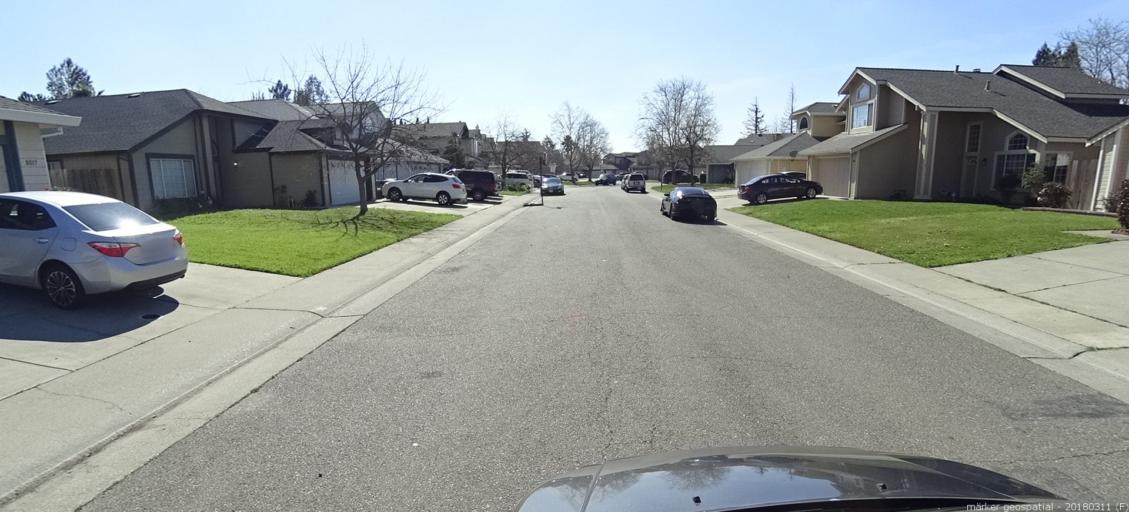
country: US
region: California
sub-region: Sacramento County
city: Florin
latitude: 38.4669
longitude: -121.3872
